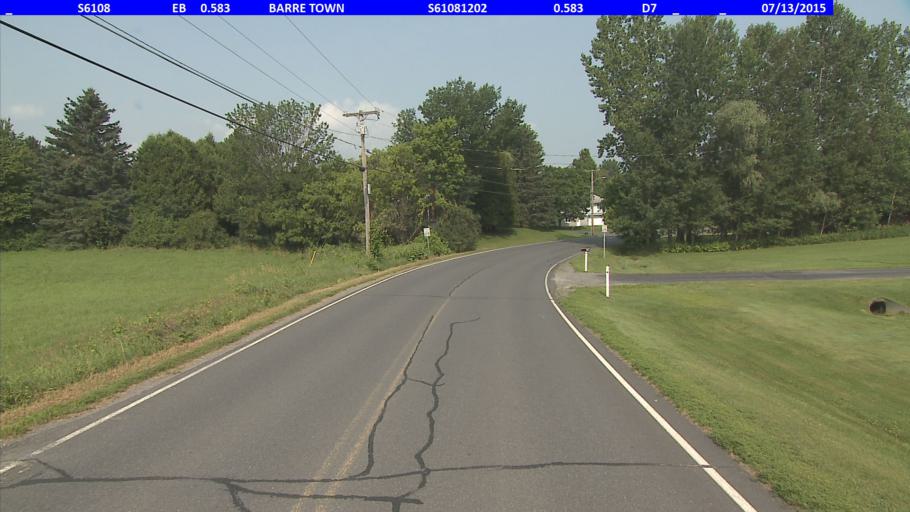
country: US
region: Vermont
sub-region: Washington County
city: Barre
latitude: 44.1863
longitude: -72.4771
